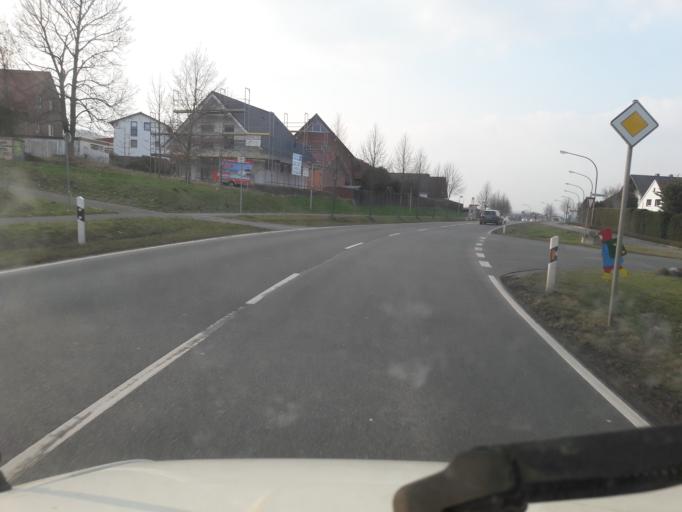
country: DE
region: North Rhine-Westphalia
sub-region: Regierungsbezirk Detmold
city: Huellhorst
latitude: 52.2986
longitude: 8.7087
